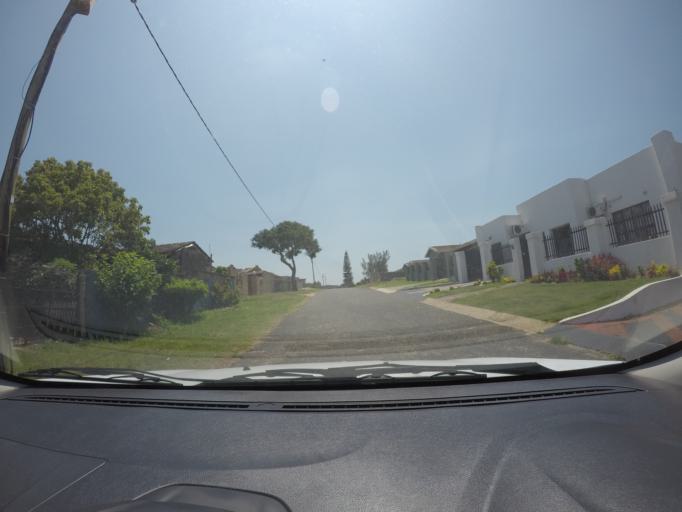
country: ZA
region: KwaZulu-Natal
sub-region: uThungulu District Municipality
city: eSikhawini
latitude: -28.8711
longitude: 31.9210
